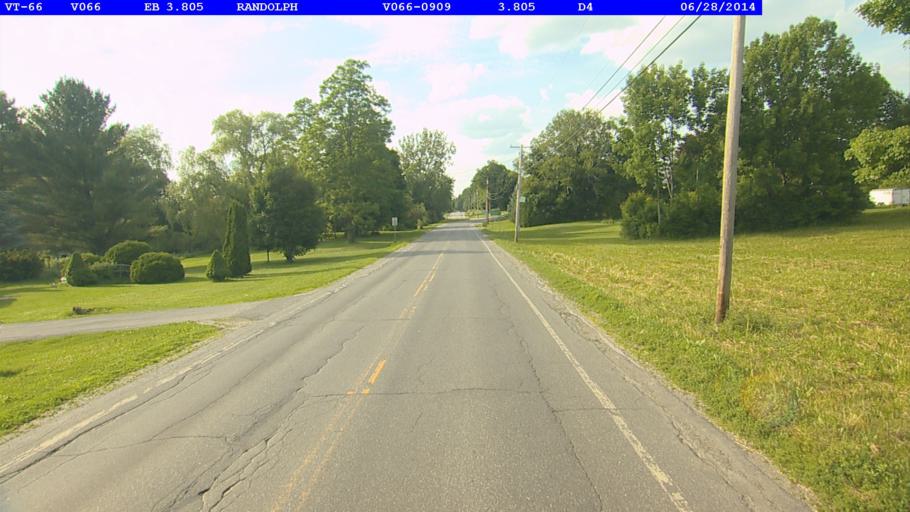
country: US
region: Vermont
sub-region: Orange County
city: Randolph
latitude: 43.9474
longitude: -72.6083
